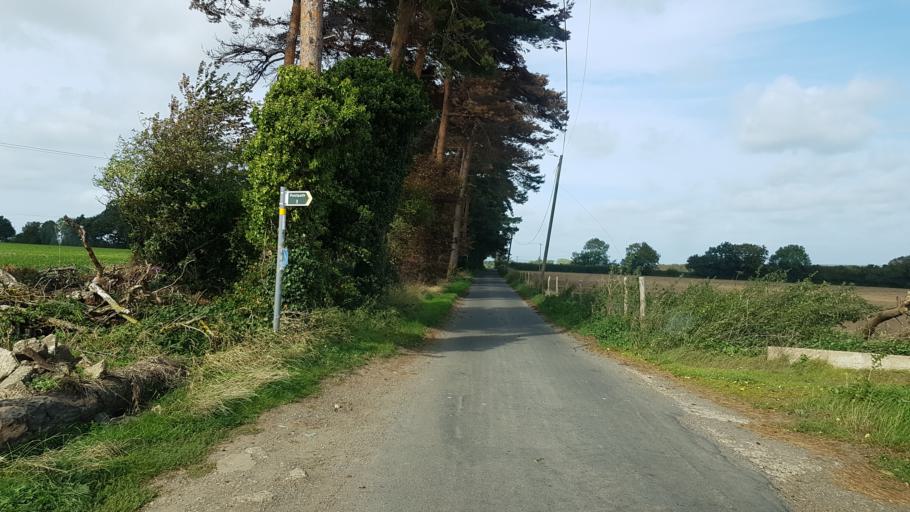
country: GB
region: England
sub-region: Kent
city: Harrietsham
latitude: 51.2393
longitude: 0.6201
